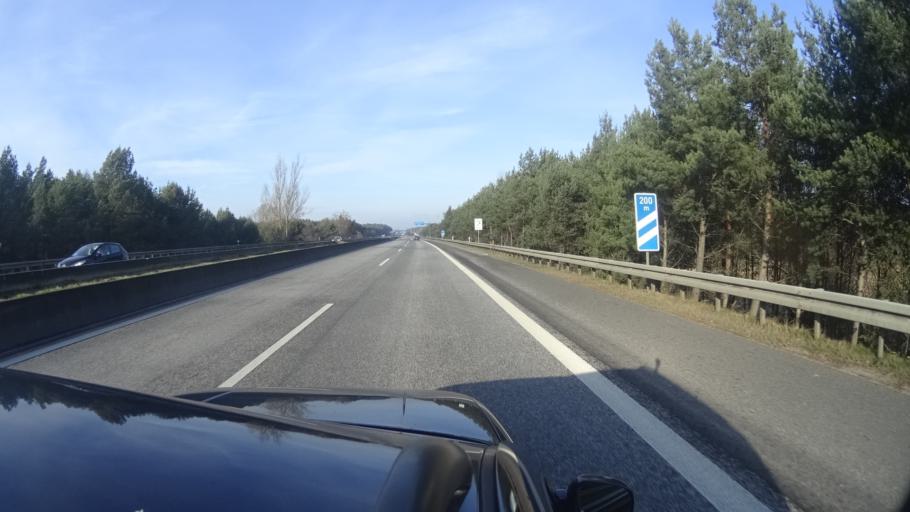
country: DE
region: Brandenburg
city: Hohen Neuendorf
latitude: 52.6752
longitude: 13.2307
